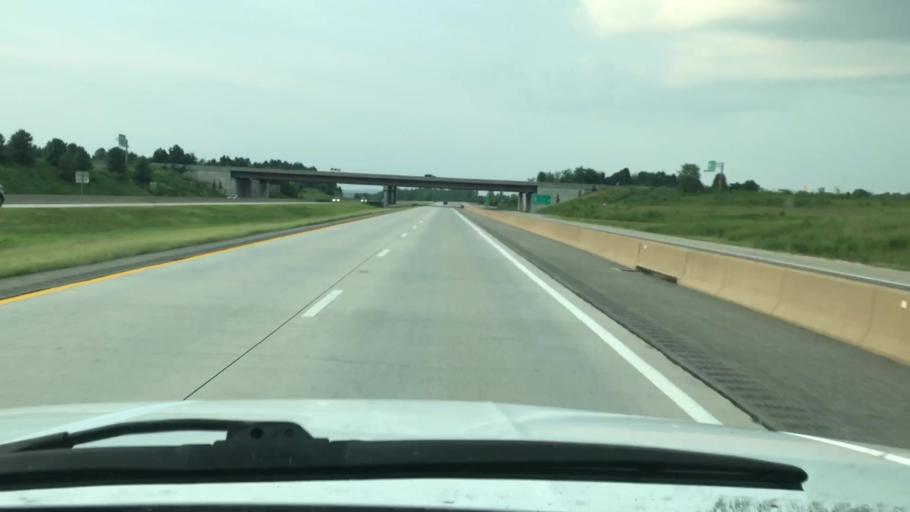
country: US
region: Virginia
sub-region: Chesterfield County
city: Brandermill
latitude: 37.5076
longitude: -77.6868
